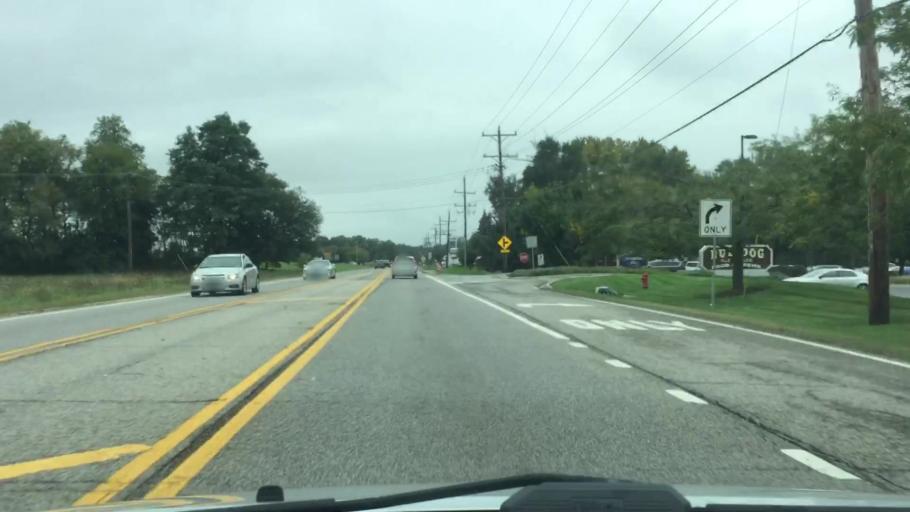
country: US
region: Illinois
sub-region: McHenry County
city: McHenry
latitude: 42.3075
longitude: -88.2816
